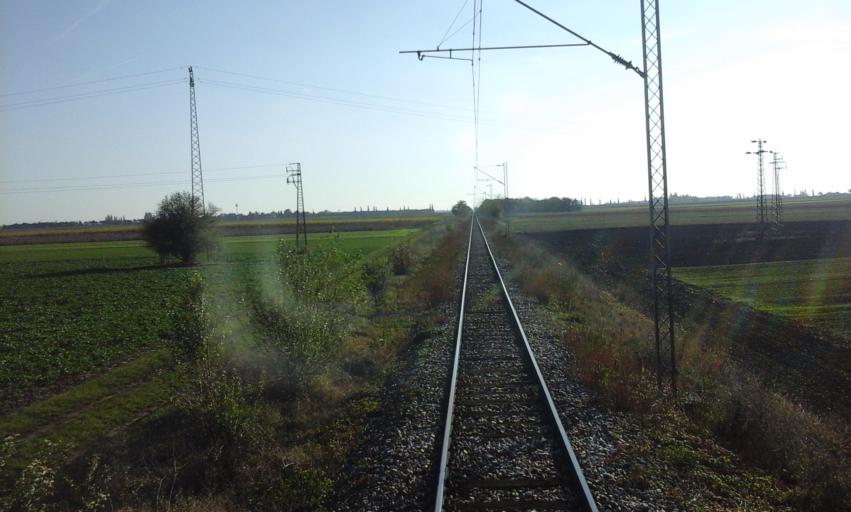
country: RS
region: Autonomna Pokrajina Vojvodina
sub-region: Severnobacki Okrug
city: Backa Topola
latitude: 45.7920
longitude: 19.6474
